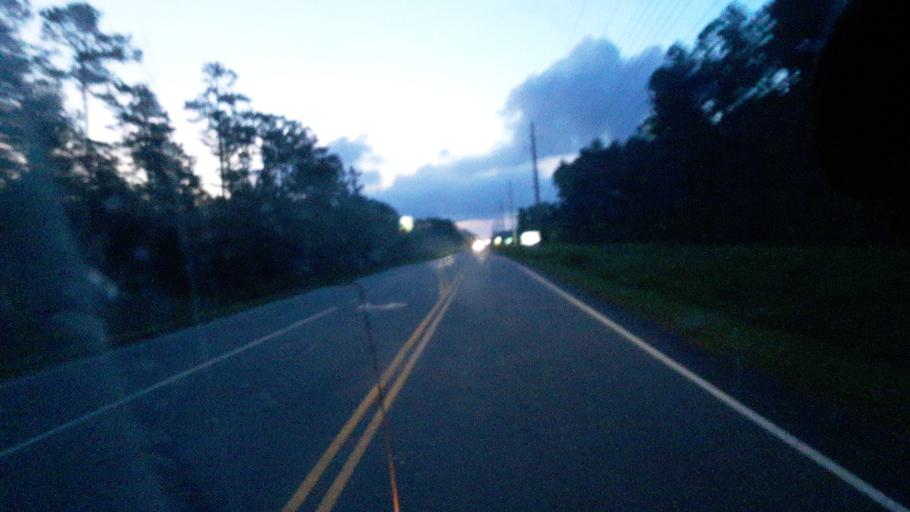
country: US
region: North Carolina
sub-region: Brunswick County
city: Oak Island
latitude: 33.9889
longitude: -78.2011
